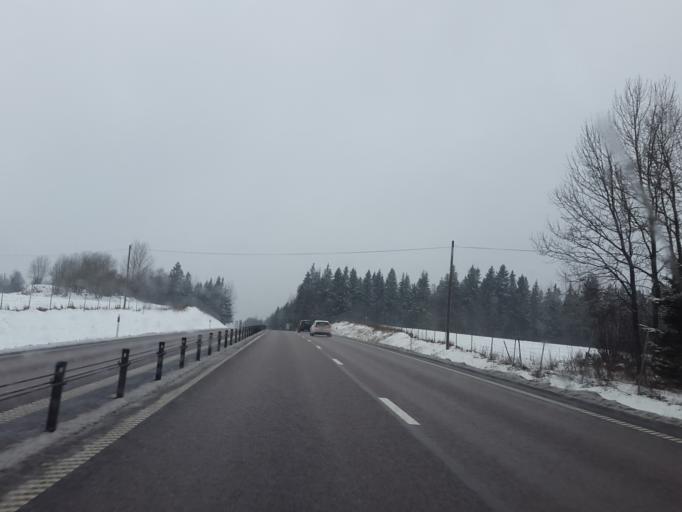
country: SE
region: Vaestra Goetaland
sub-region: Ulricehamns Kommun
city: Ulricehamn
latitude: 57.7969
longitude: 13.5823
